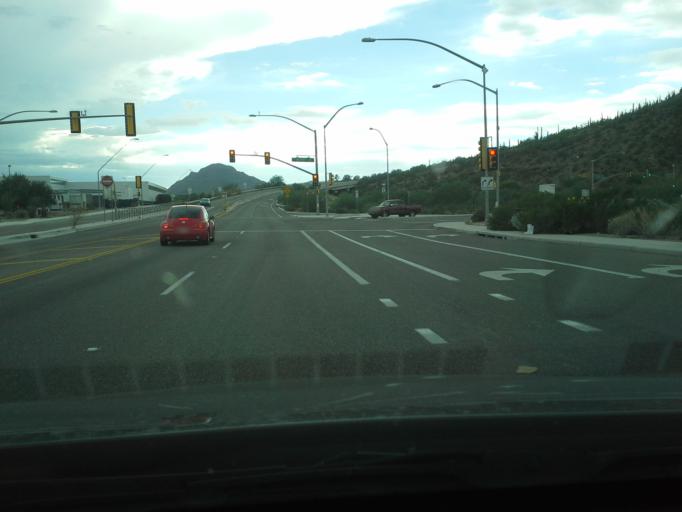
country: US
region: Arizona
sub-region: Pima County
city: South Tucson
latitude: 32.2061
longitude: -110.9897
